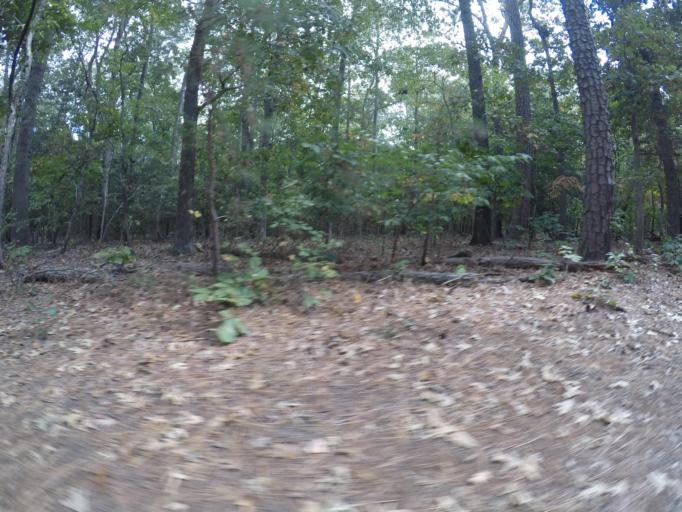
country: US
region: Delaware
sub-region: Sussex County
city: Rehoboth Beach
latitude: 38.7179
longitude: -75.1055
